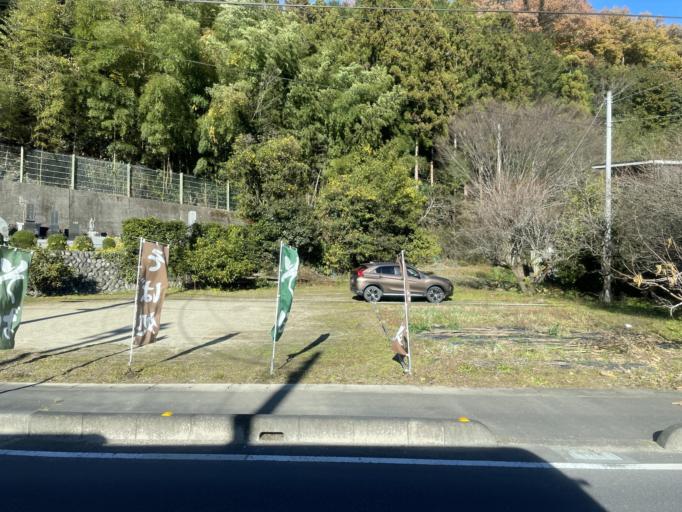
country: JP
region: Saitama
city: Yorii
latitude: 36.0559
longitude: 139.2013
